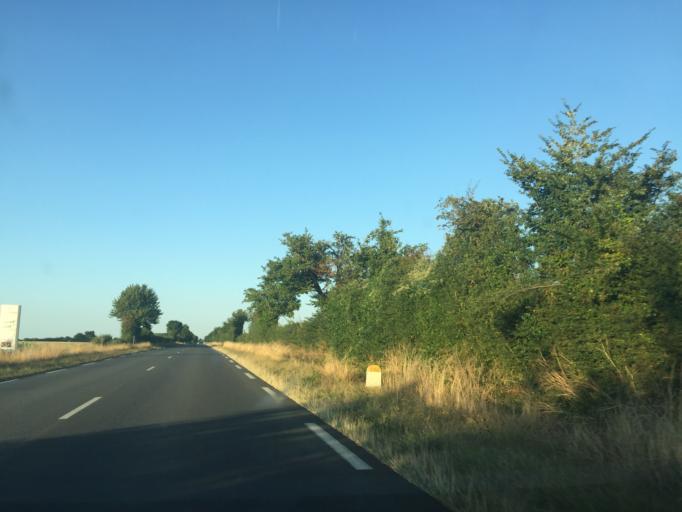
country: FR
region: Poitou-Charentes
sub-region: Departement de la Vienne
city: Saint-Sauvant
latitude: 46.3481
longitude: -0.0022
